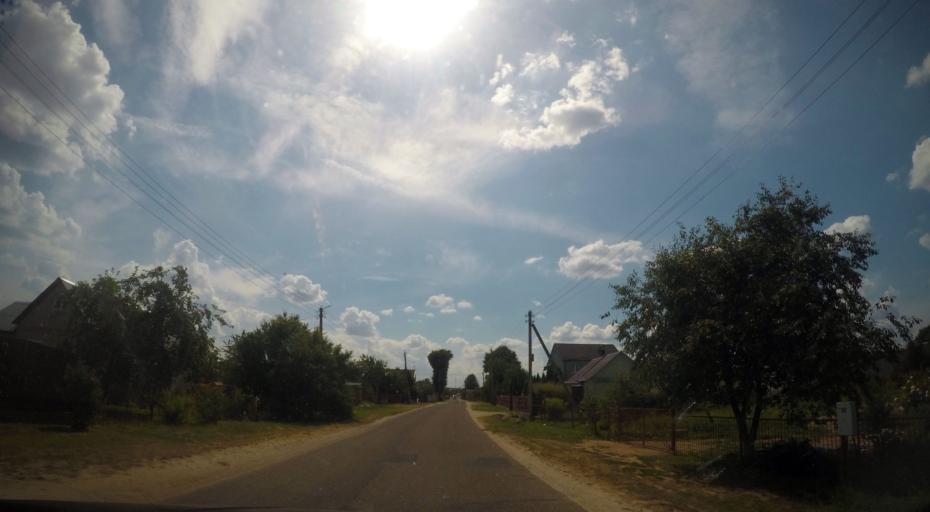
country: BY
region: Grodnenskaya
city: Hrodna
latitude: 53.6309
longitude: 23.8430
